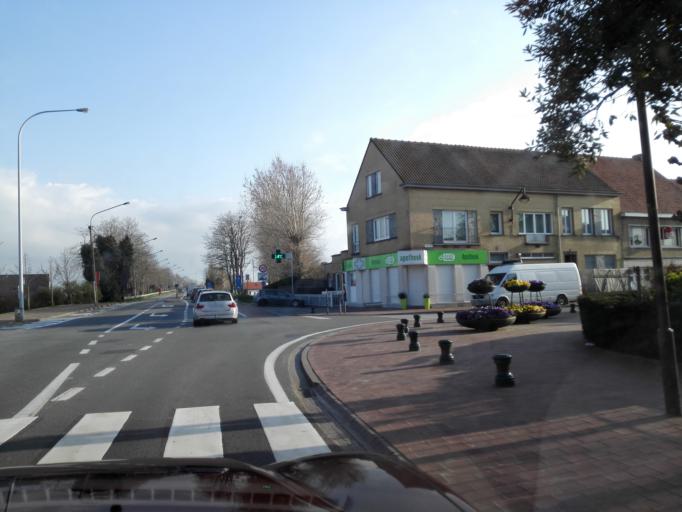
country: BE
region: Flanders
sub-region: Provincie West-Vlaanderen
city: De Panne
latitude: 51.0753
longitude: 2.6034
